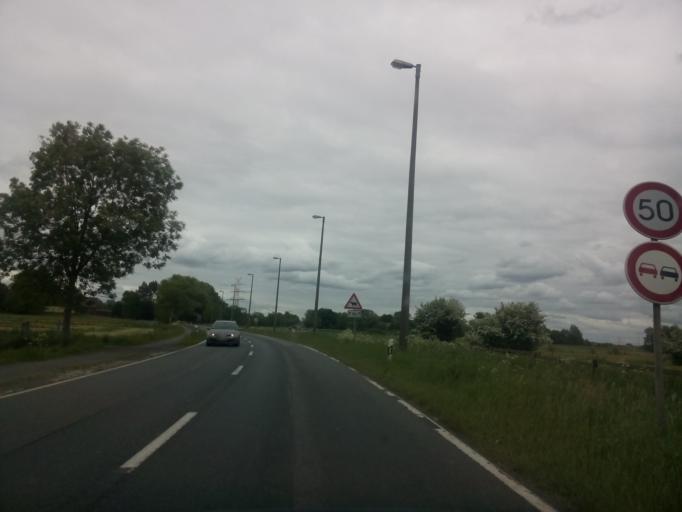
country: DE
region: Lower Saxony
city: Stuhr
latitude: 53.0769
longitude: 8.7243
